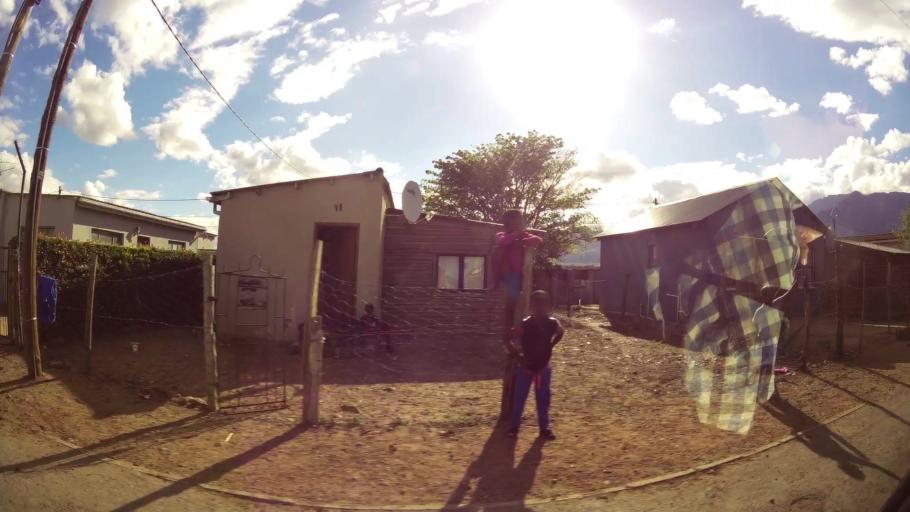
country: ZA
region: Western Cape
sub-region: Overberg District Municipality
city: Swellendam
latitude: -34.0446
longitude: 20.4397
